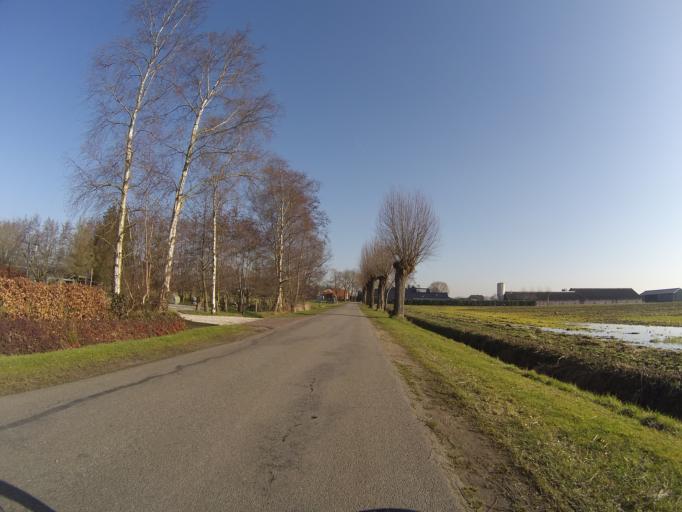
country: NL
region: Gelderland
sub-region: Gemeente Barneveld
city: Zwartebroek
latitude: 52.1814
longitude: 5.4911
